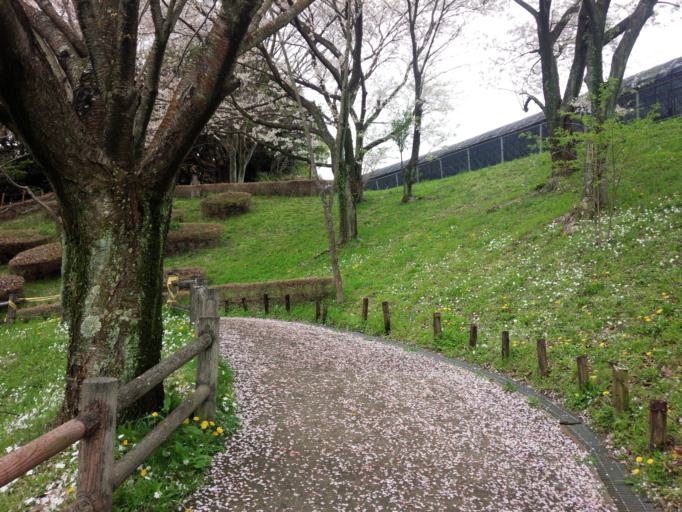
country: JP
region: Shizuoka
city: Shizuoka-shi
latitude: 34.9970
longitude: 138.4642
